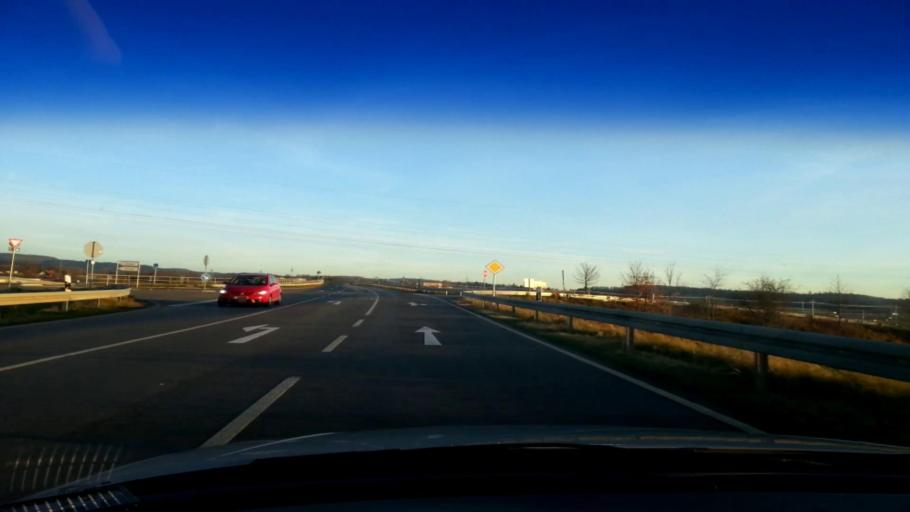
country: DE
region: Bavaria
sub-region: Upper Franconia
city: Ebensfeld
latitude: 50.0613
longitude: 10.9484
